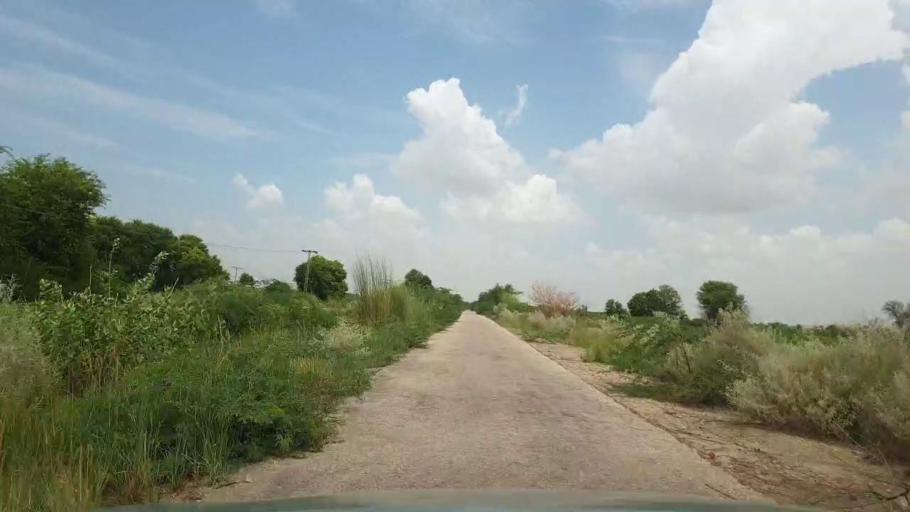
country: PK
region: Sindh
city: Bozdar
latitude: 27.0236
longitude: 68.9494
